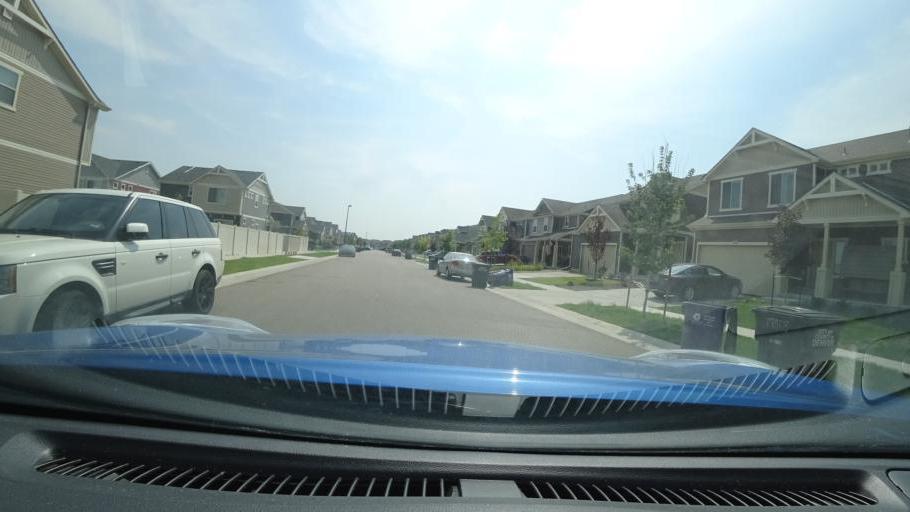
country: US
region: Colorado
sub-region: Adams County
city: Aurora
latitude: 39.7768
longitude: -104.7799
